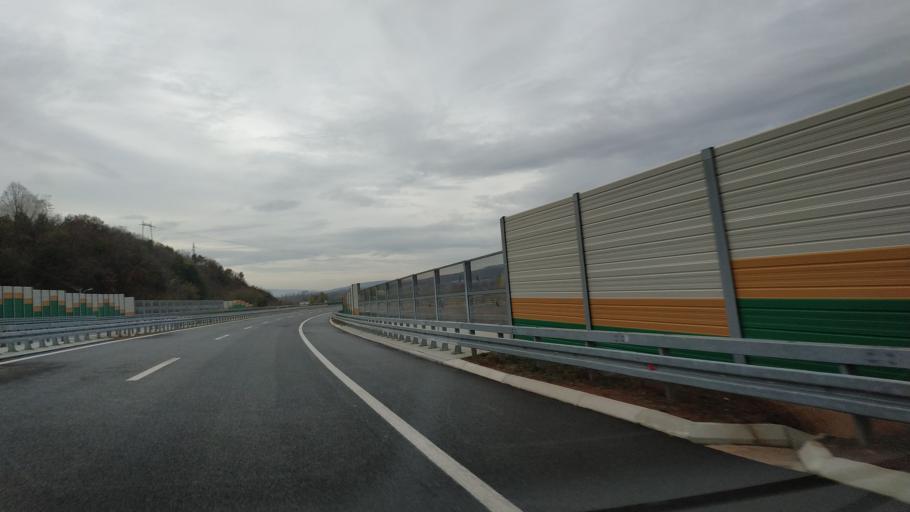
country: RS
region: Central Serbia
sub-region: Nisavski Okrug
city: Niska Banja
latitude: 43.3006
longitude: 22.0477
